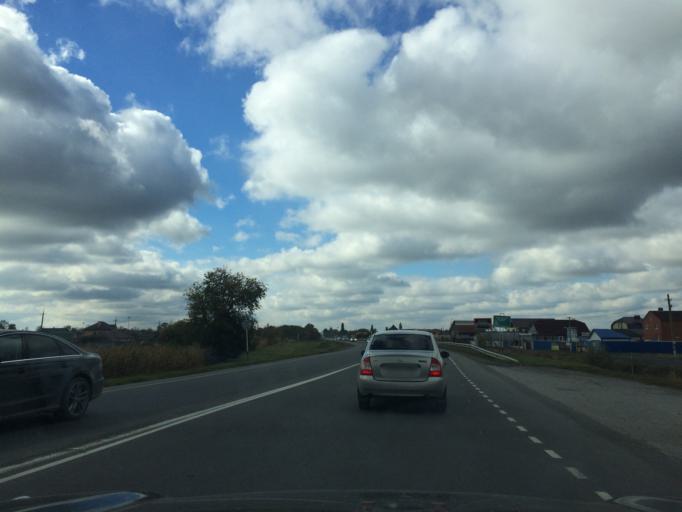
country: RU
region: Rostov
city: Bataysk
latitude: 47.1139
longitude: 39.6608
